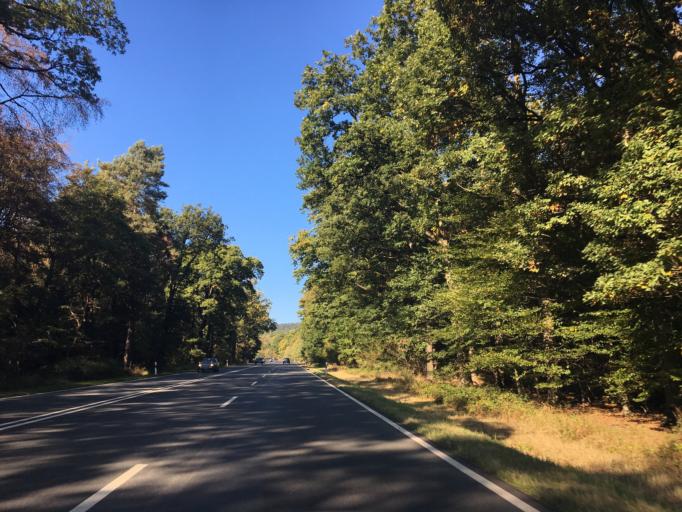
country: DE
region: Hesse
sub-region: Regierungsbezirk Darmstadt
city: Bad Homburg vor der Hoehe
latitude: 50.2543
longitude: 8.5890
